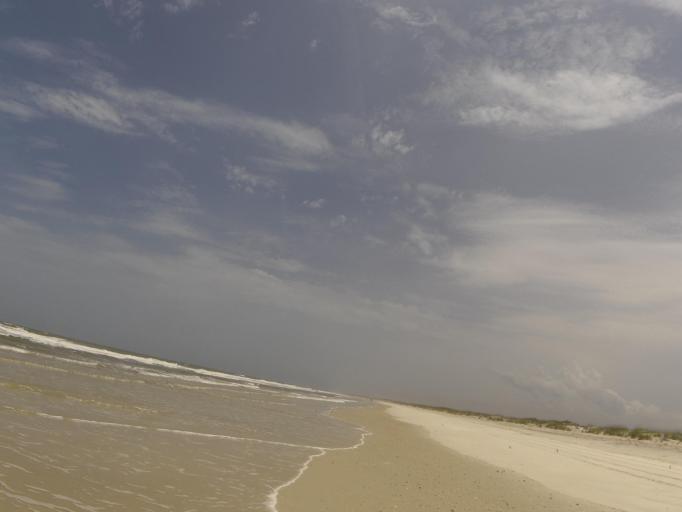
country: US
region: Florida
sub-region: Saint Johns County
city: Saint Augustine
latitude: 29.8993
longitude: -81.2766
